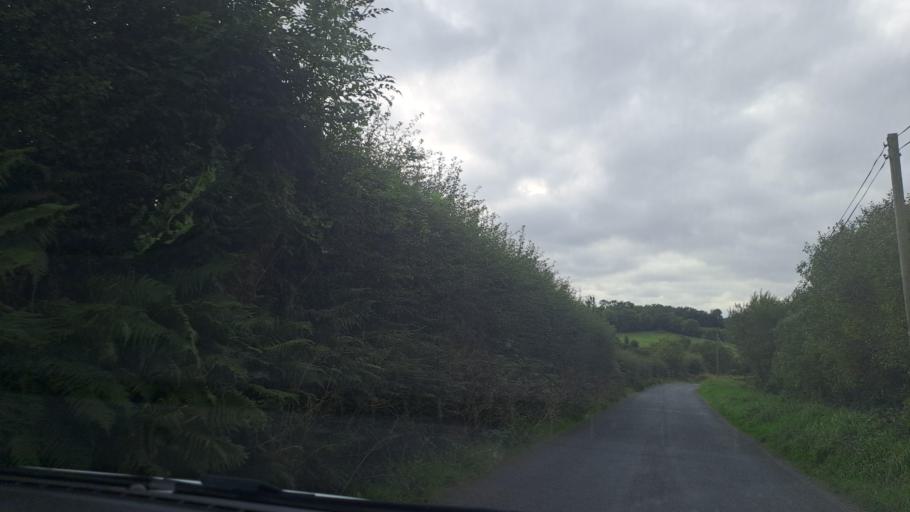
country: IE
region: Ulster
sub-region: An Cabhan
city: Bailieborough
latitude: 53.9395
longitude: -6.9114
